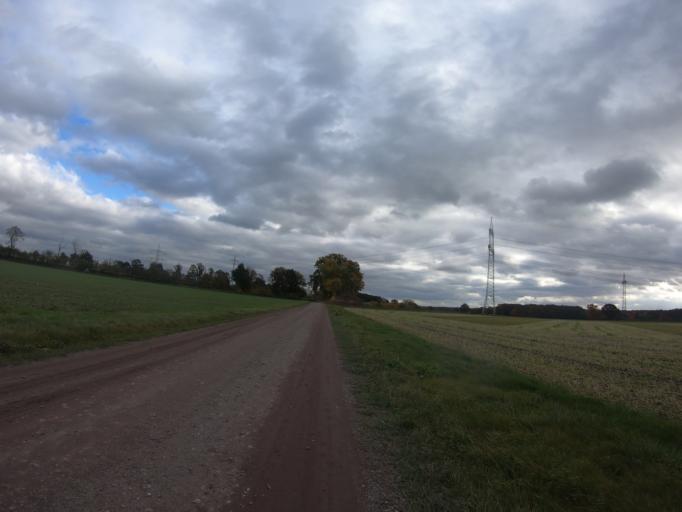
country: DE
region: Lower Saxony
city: Vordorf
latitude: 52.3716
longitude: 10.5036
